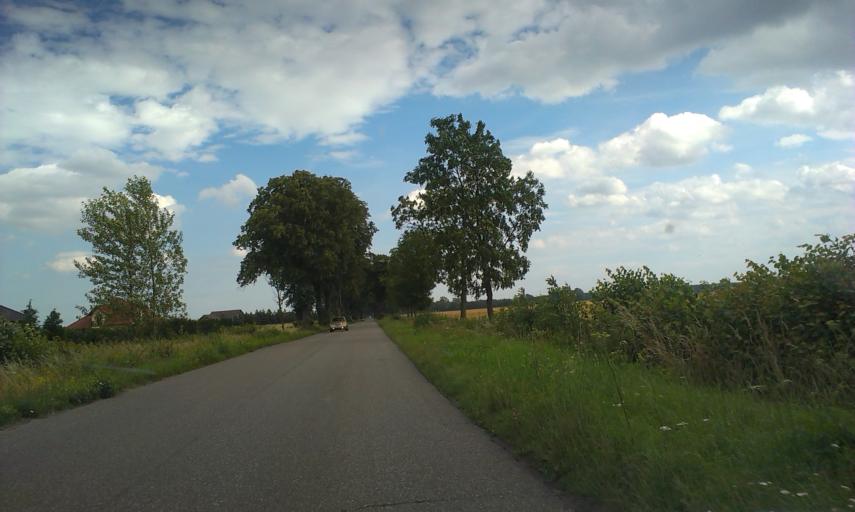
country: PL
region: Greater Poland Voivodeship
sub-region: Powiat zlotowski
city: Zlotow
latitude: 53.3881
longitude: 17.0120
